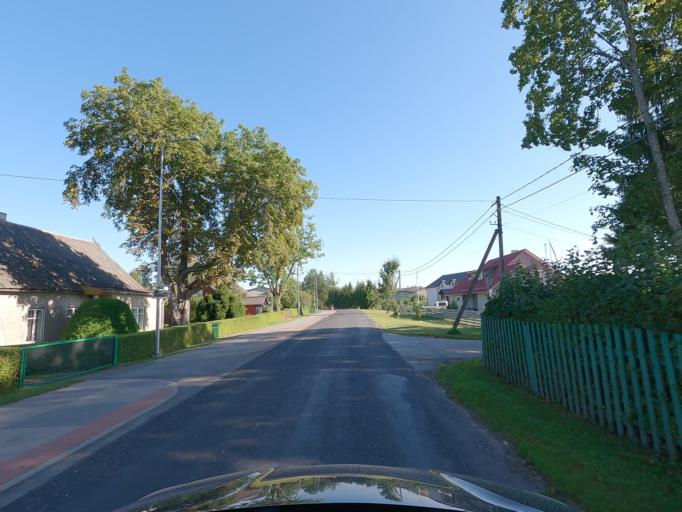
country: EE
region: Raplamaa
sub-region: Rapla vald
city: Rapla
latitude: 59.0112
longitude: 24.7866
